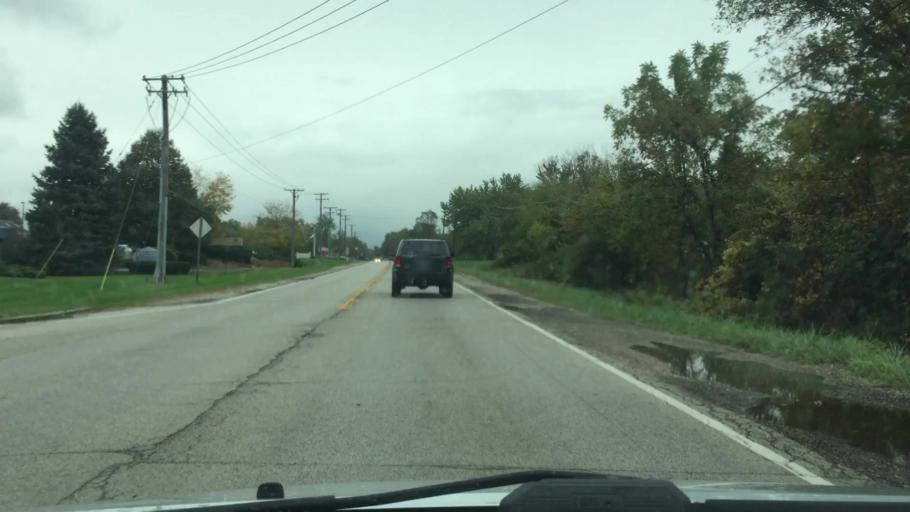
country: US
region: Illinois
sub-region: McHenry County
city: Richmond
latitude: 42.4683
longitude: -88.3070
